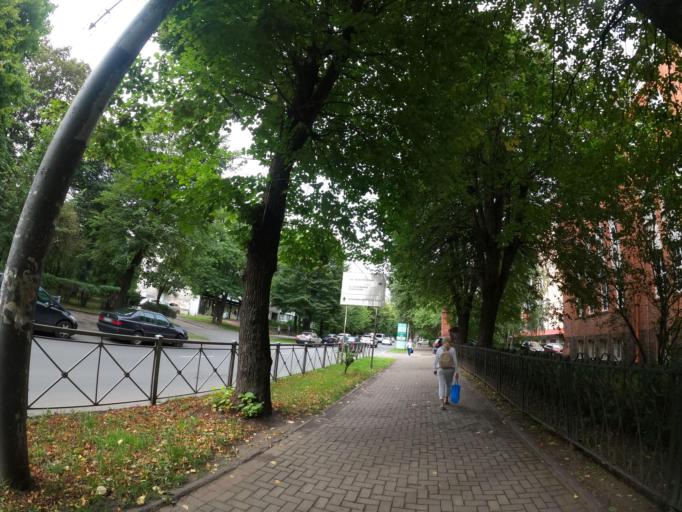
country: RU
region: Kaliningrad
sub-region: Gorod Kaliningrad
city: Kaliningrad
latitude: 54.7218
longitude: 20.4823
